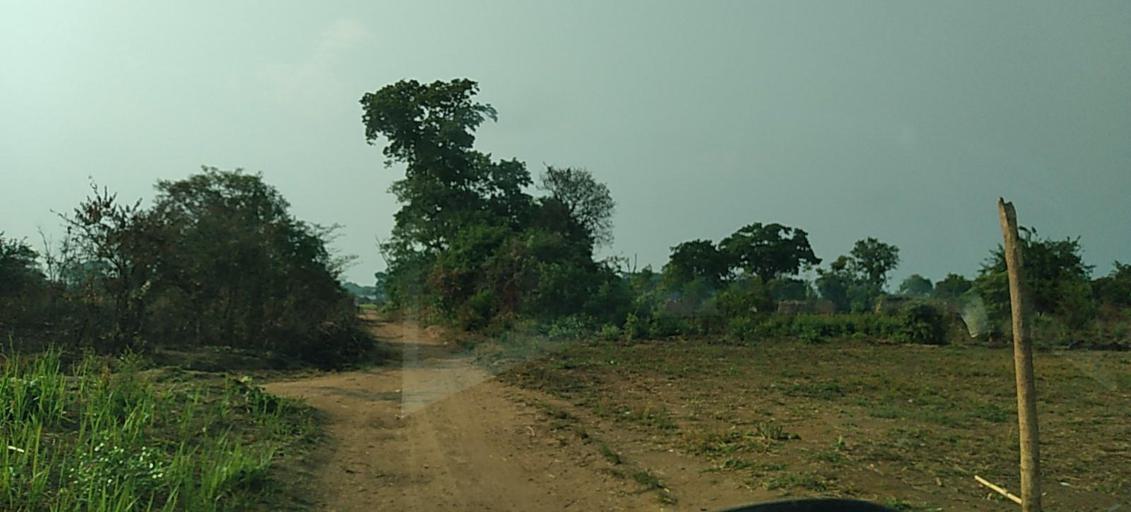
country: ZM
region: North-Western
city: Solwezi
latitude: -12.3645
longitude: 26.5547
